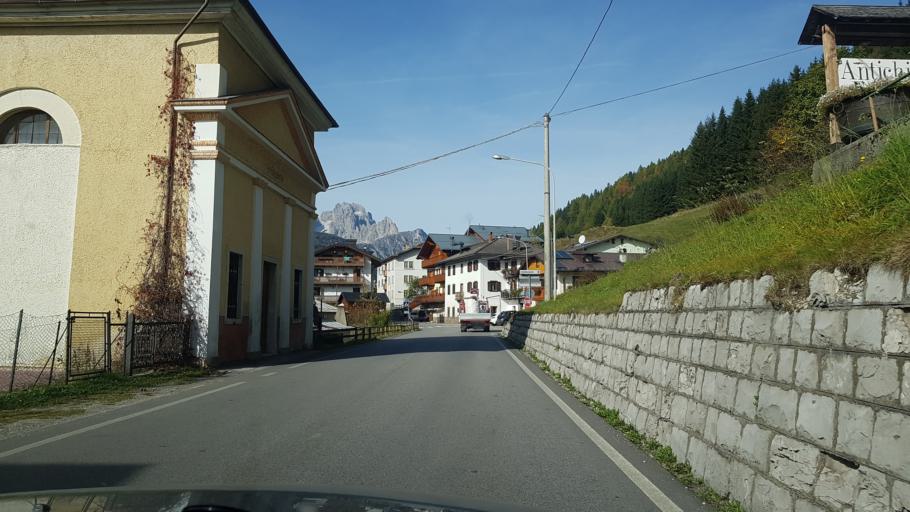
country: IT
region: Veneto
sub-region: Provincia di Belluno
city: Candide
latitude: 46.5967
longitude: 12.4989
